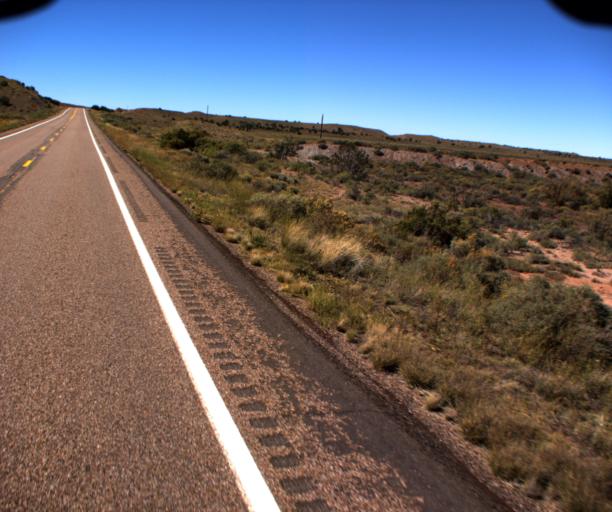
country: US
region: Arizona
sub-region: Apache County
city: Saint Johns
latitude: 34.5871
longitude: -109.5553
